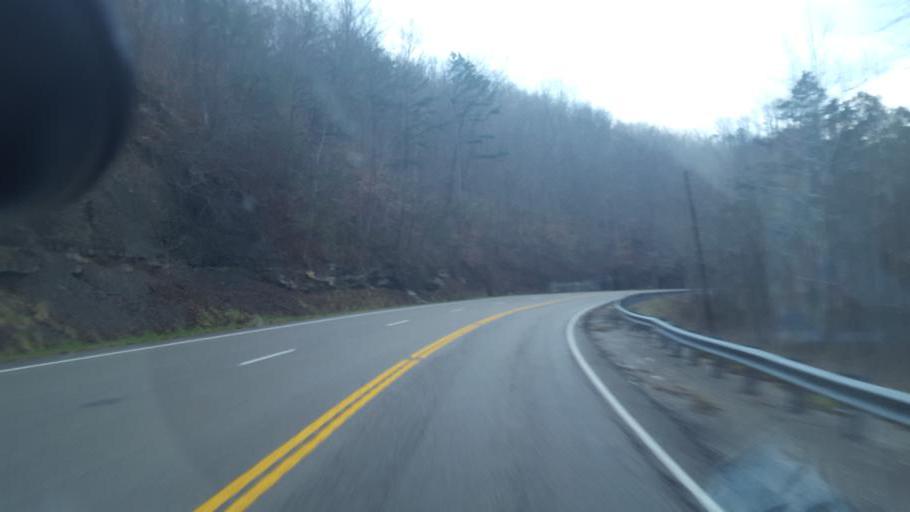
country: US
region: Kentucky
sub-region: Rockcastle County
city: Mount Vernon
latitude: 37.2999
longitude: -84.2316
